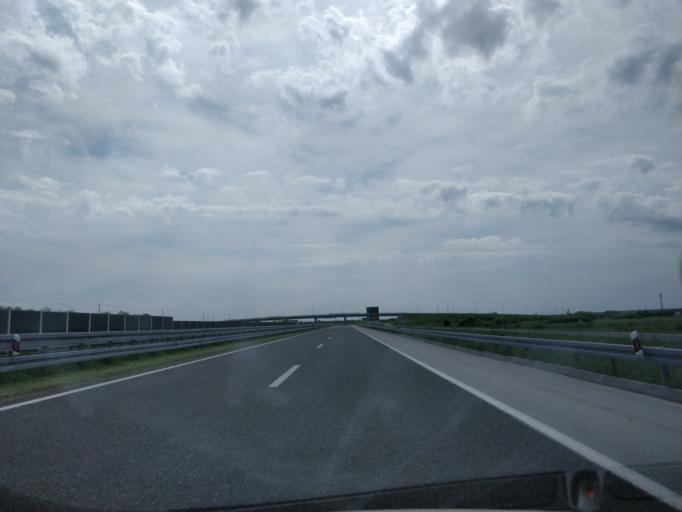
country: HR
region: Zagrebacka
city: Gradici
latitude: 45.7016
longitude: 16.0553
